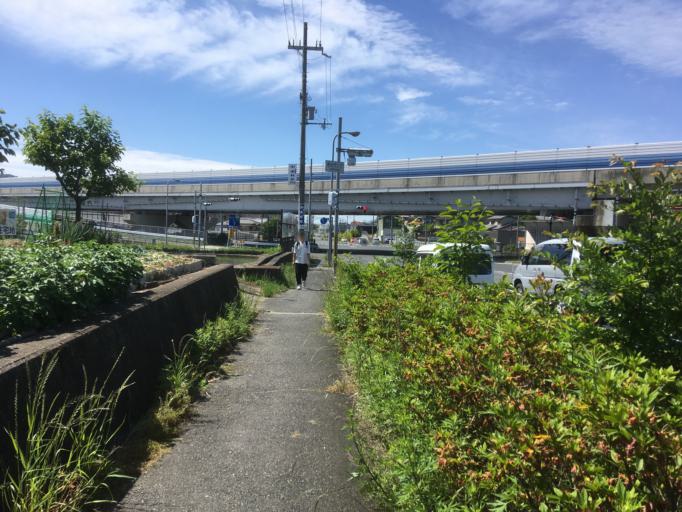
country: JP
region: Nara
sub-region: Ikoma-shi
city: Ikoma
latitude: 34.6735
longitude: 135.7067
